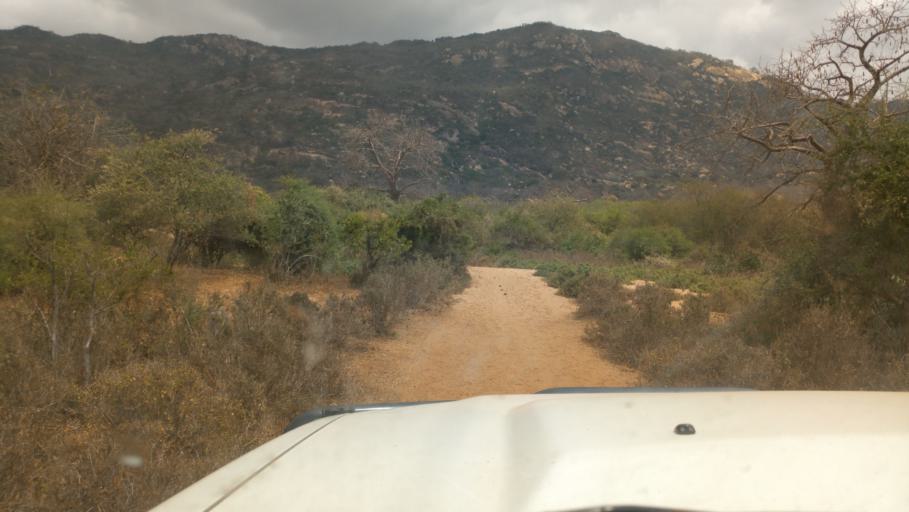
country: KE
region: Kitui
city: Kitui
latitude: -1.8840
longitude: 38.3704
